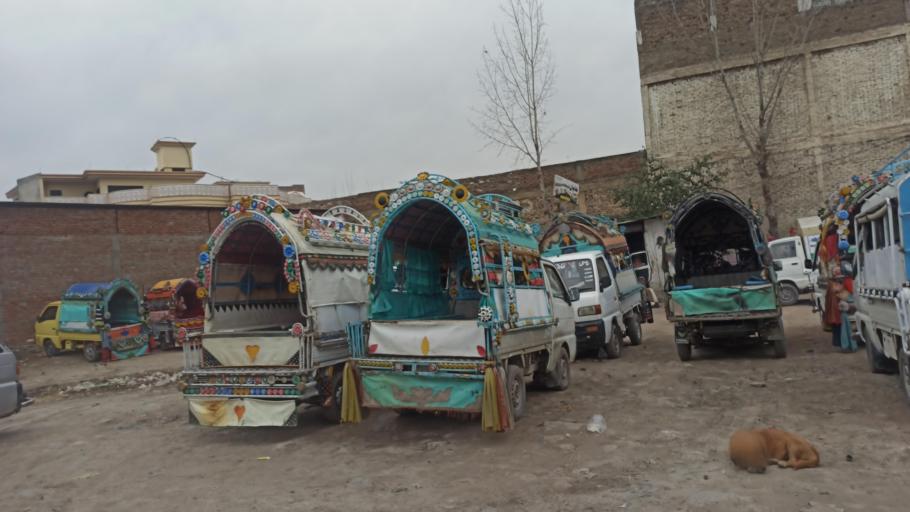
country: PK
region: Khyber Pakhtunkhwa
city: Mingora
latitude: 34.7731
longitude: 72.3523
